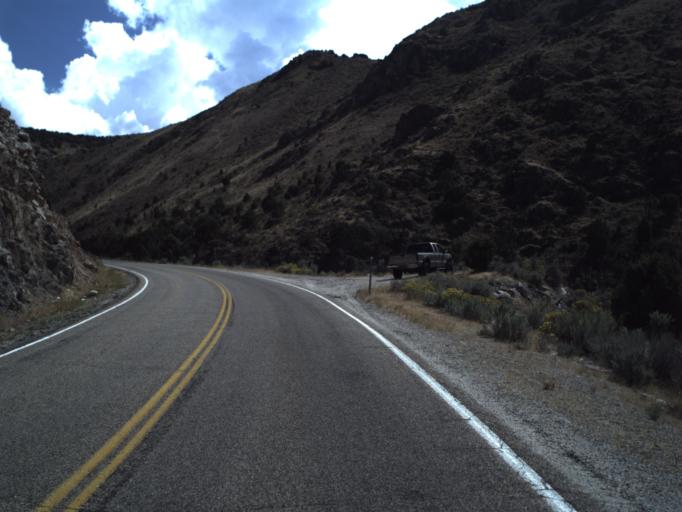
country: US
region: Utah
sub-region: Rich County
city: Randolph
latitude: 41.8250
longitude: -111.3096
